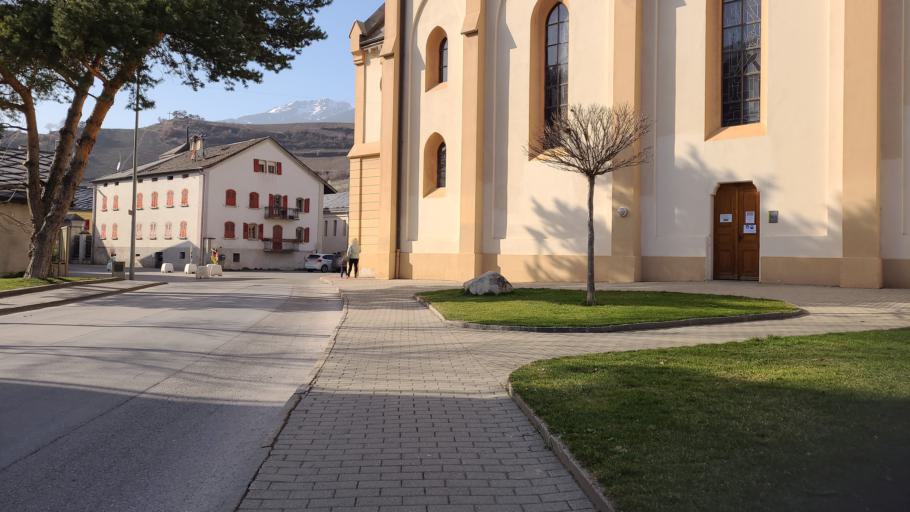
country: CH
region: Valais
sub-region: Leuk District
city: Salgesch
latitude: 46.3116
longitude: 7.5711
